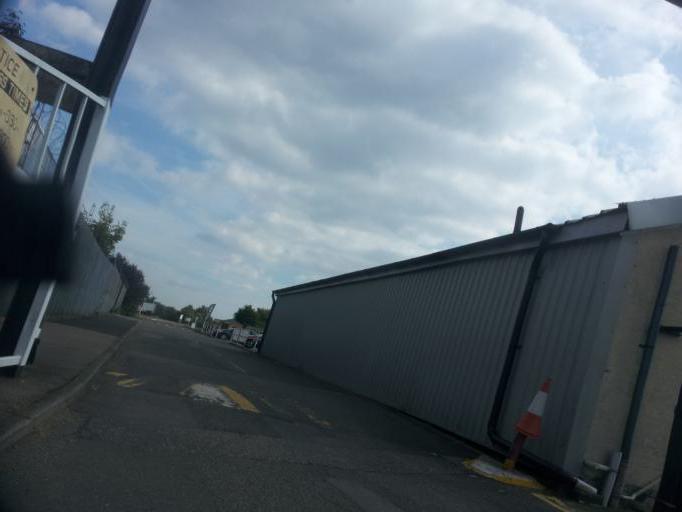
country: GB
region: England
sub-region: Kent
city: Boxley
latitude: 51.3405
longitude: 0.5586
